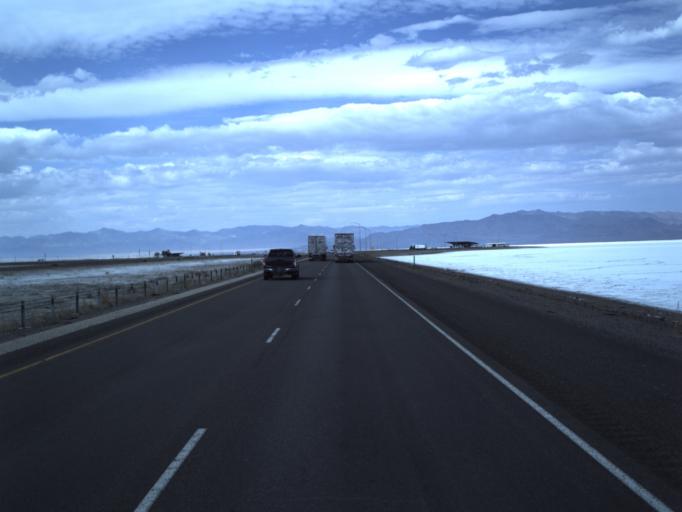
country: US
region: Utah
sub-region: Tooele County
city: Wendover
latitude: 40.7392
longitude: -113.8431
